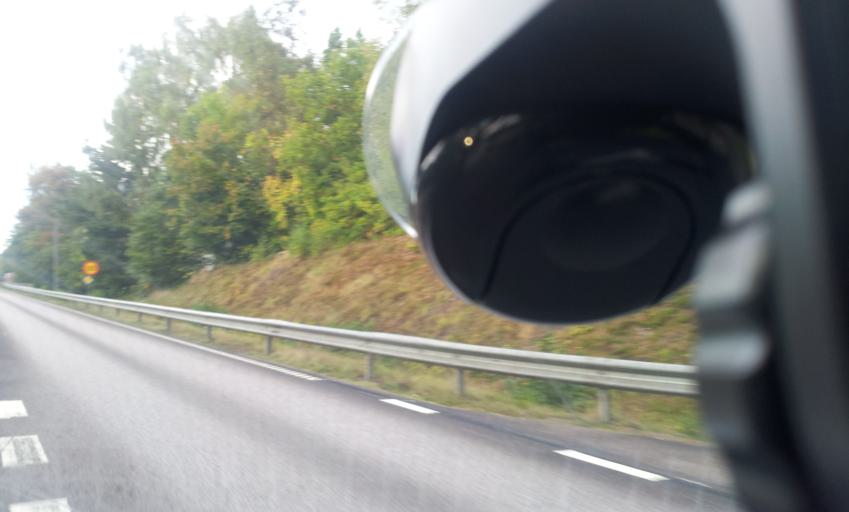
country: SE
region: Kalmar
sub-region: Oskarshamns Kommun
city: Oskarshamn
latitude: 57.3056
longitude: 16.4618
